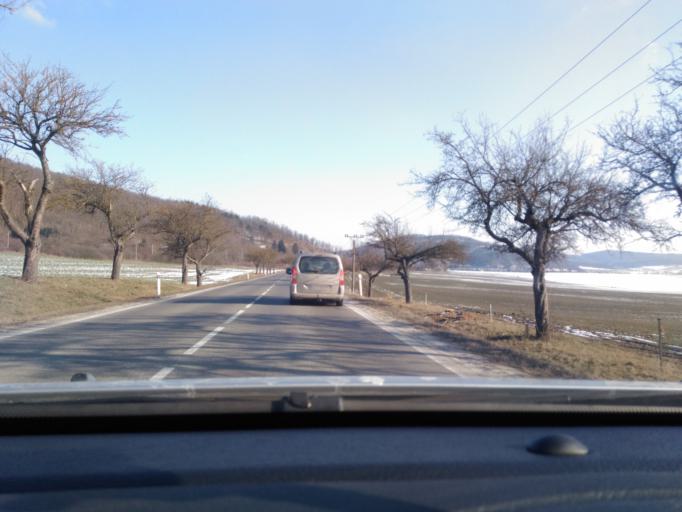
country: CZ
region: South Moravian
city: Kurim
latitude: 49.3065
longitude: 16.5061
